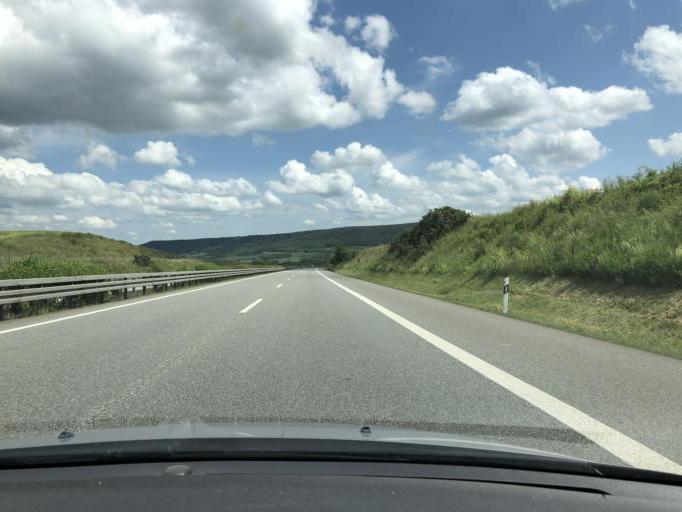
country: DE
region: Thuringia
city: Sollstedt
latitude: 51.4197
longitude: 10.5495
